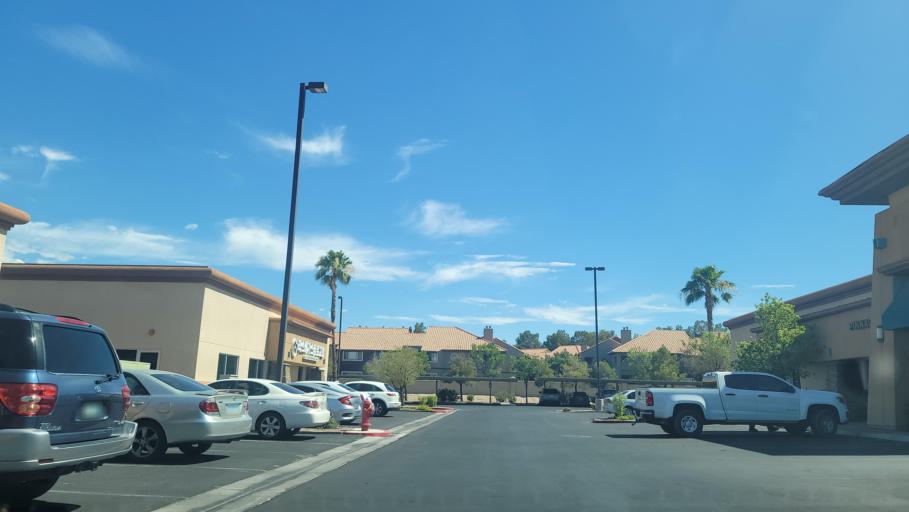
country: US
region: Nevada
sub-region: Clark County
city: Spring Valley
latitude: 36.0988
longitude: -115.2413
